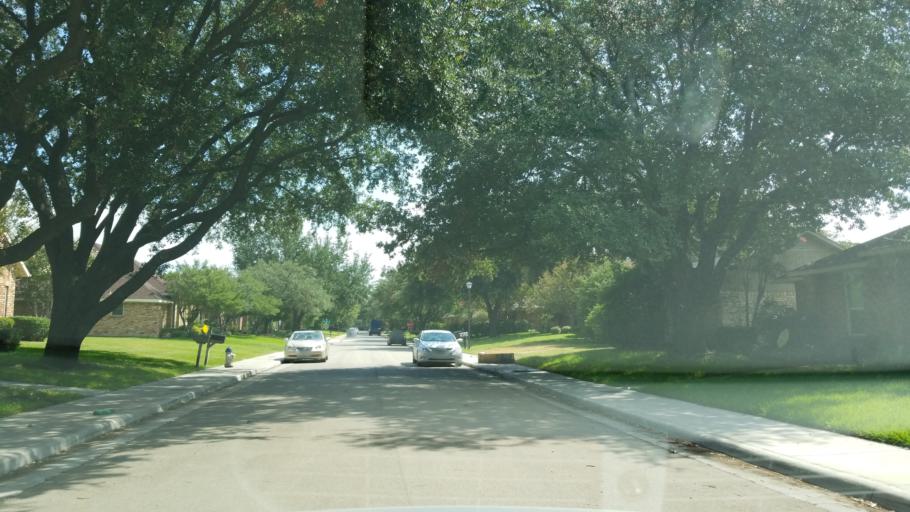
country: US
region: Texas
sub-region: Dallas County
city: Addison
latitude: 32.9573
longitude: -96.8035
